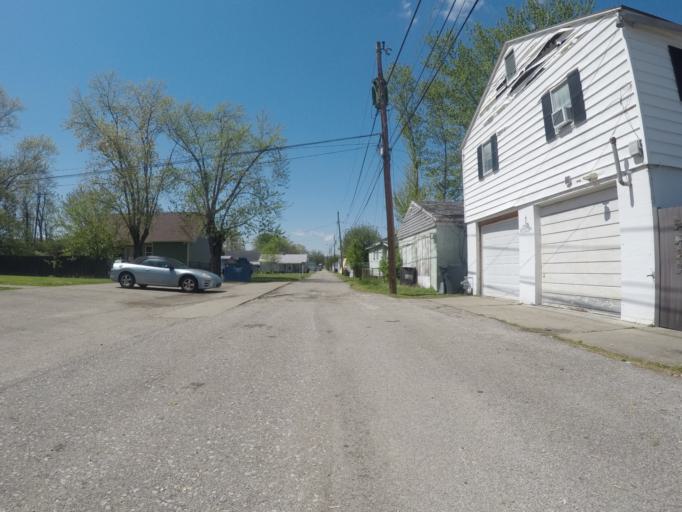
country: US
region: West Virginia
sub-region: Wayne County
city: Ceredo
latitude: 38.3954
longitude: -82.5668
